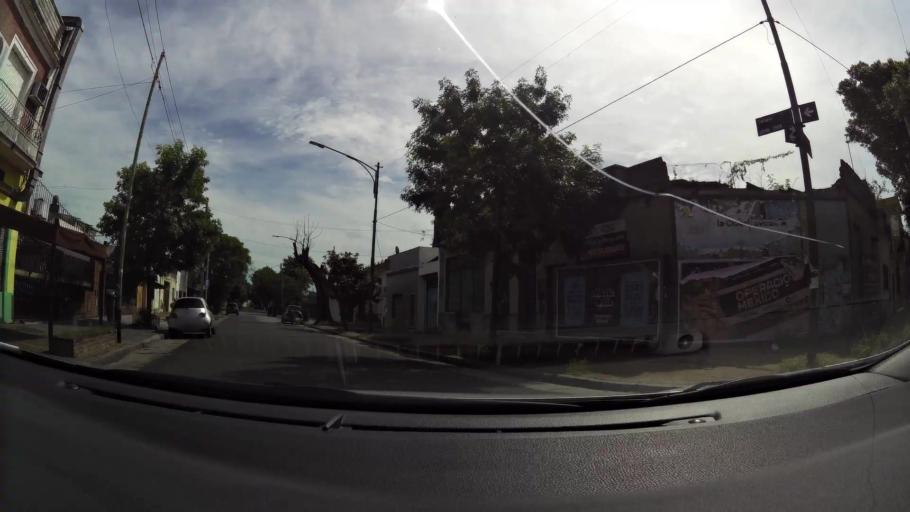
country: AR
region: Buenos Aires F.D.
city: Villa Lugano
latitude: -34.6554
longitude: -58.4284
